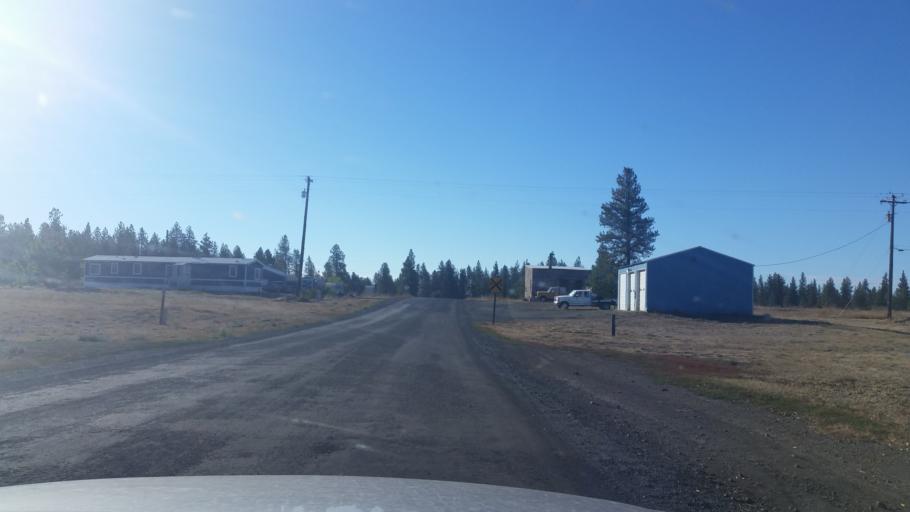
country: US
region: Washington
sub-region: Spokane County
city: Medical Lake
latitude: 47.4356
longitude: -117.7830
